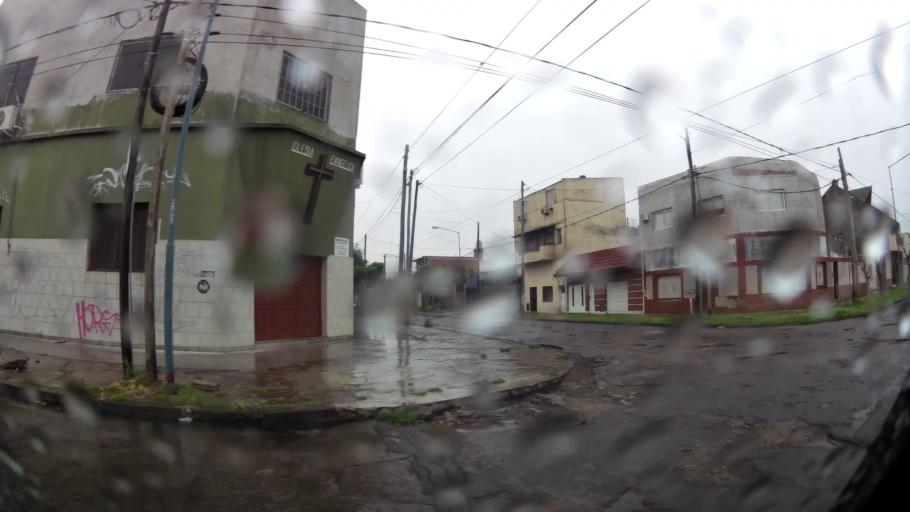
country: AR
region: Buenos Aires
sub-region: Partido de Lanus
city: Lanus
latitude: -34.7024
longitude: -58.4125
